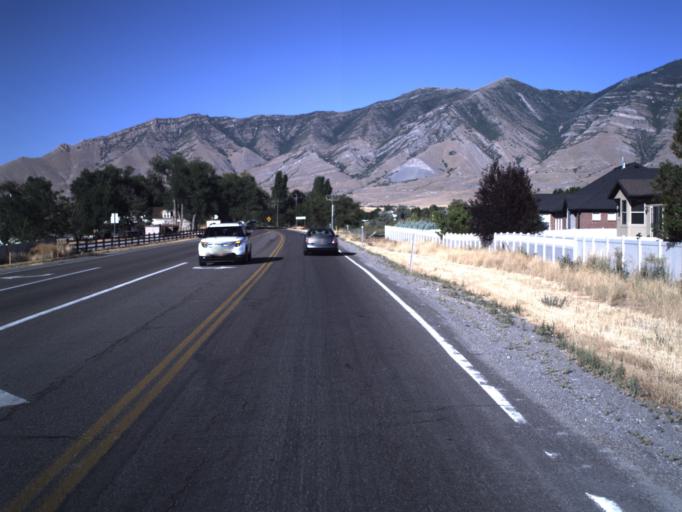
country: US
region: Utah
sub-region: Tooele County
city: Stansbury park
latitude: 40.6472
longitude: -112.3025
